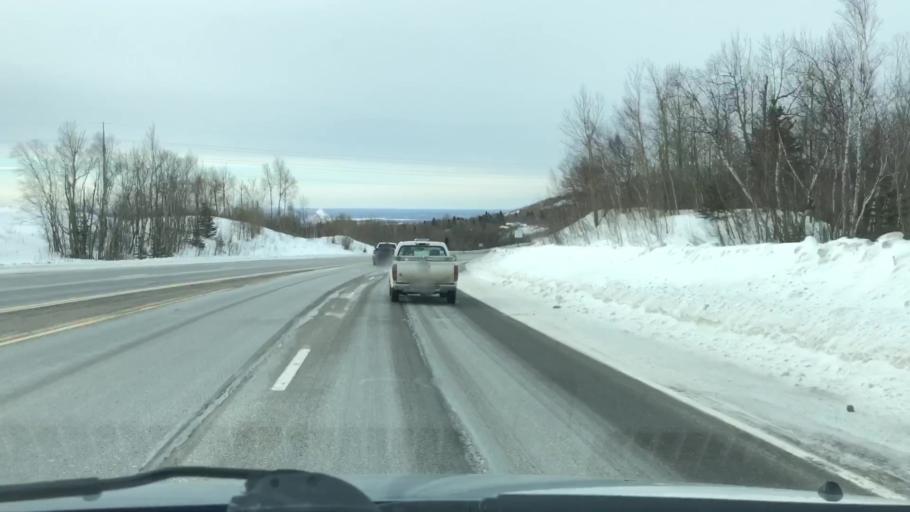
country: US
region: Minnesota
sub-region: Saint Louis County
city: Duluth
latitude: 46.7802
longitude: -92.1393
